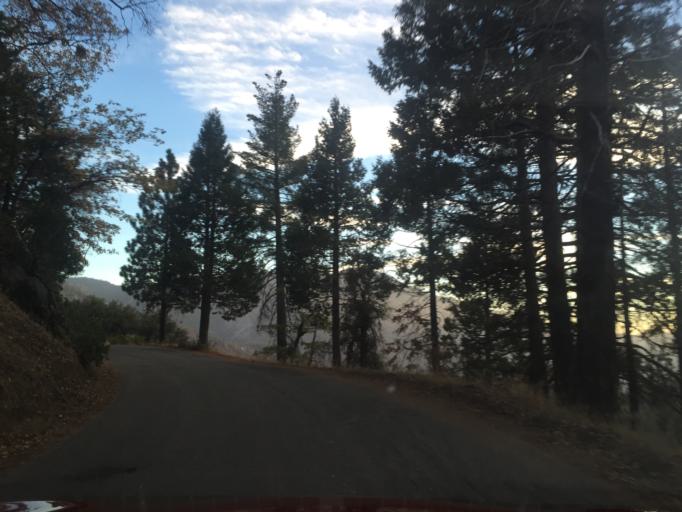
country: US
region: California
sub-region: Tulare County
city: Three Rivers
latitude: 36.4516
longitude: -118.6980
